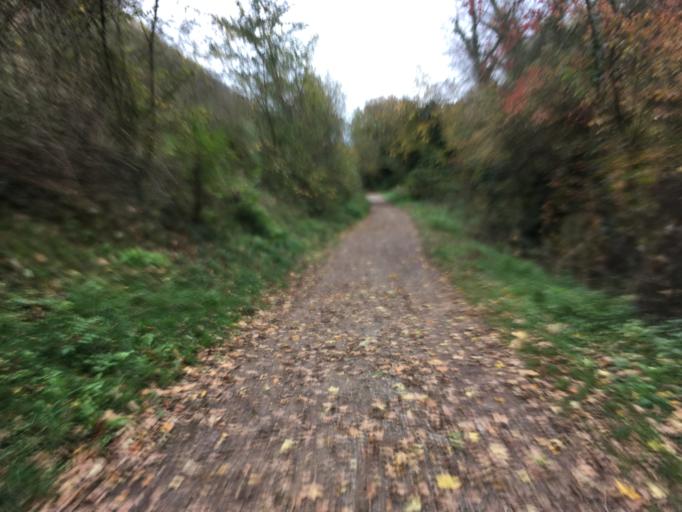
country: DE
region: Baden-Wuerttemberg
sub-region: Freiburg Region
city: Sasbach
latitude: 48.1009
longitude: 7.5924
